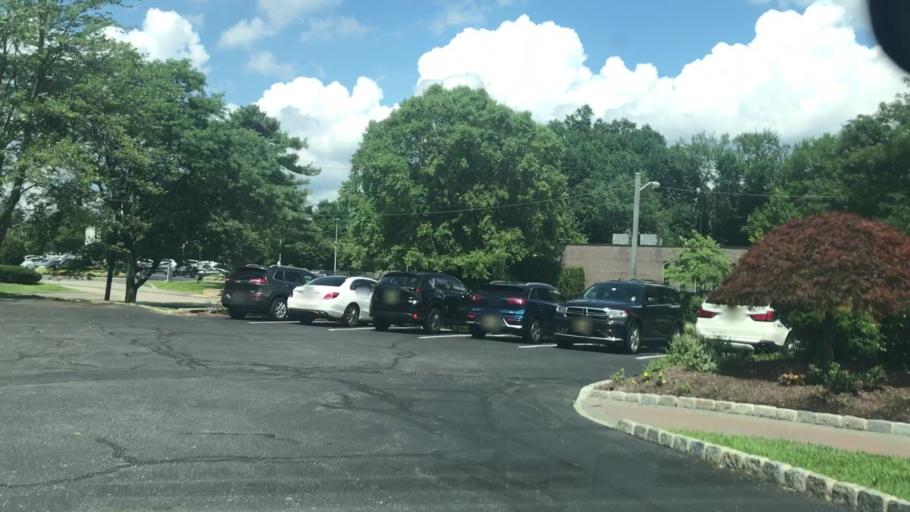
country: US
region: New Jersey
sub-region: Essex County
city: Brookdale
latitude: 40.8481
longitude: -74.1810
